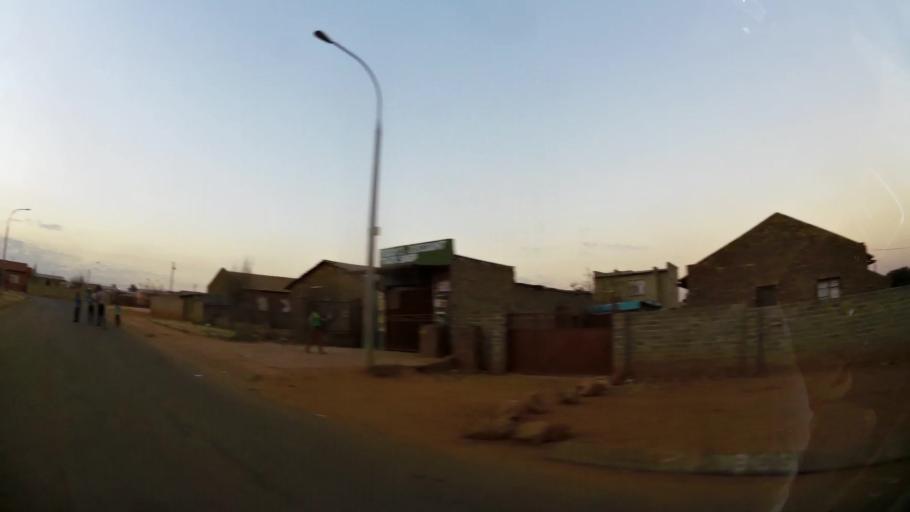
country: ZA
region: Gauteng
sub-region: West Rand District Municipality
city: Randfontein
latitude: -26.2104
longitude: 27.7093
